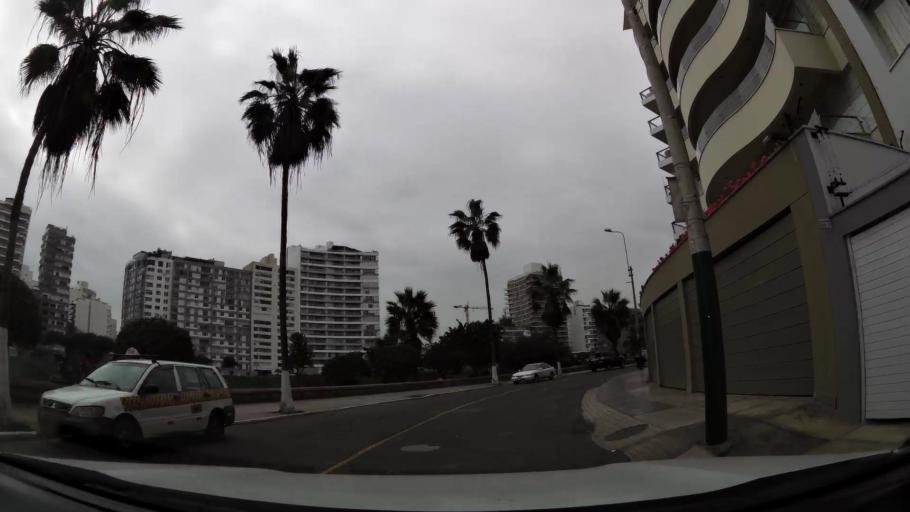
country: PE
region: Lima
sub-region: Lima
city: Surco
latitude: -12.1370
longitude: -77.0254
